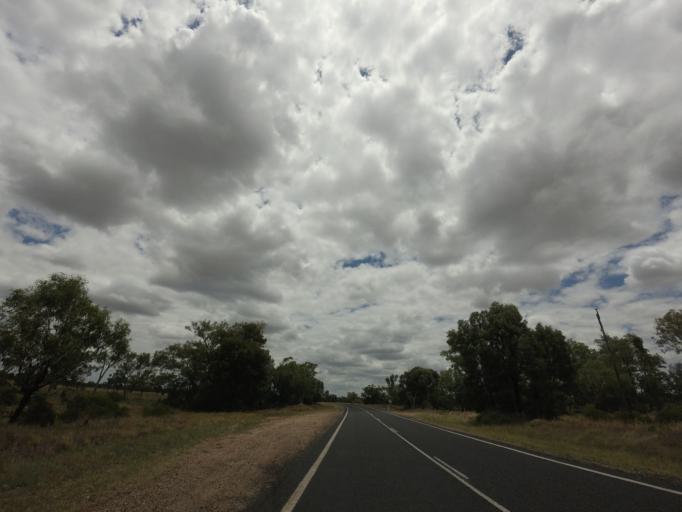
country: AU
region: Queensland
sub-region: Goondiwindi
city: Goondiwindi
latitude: -28.4831
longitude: 150.2937
